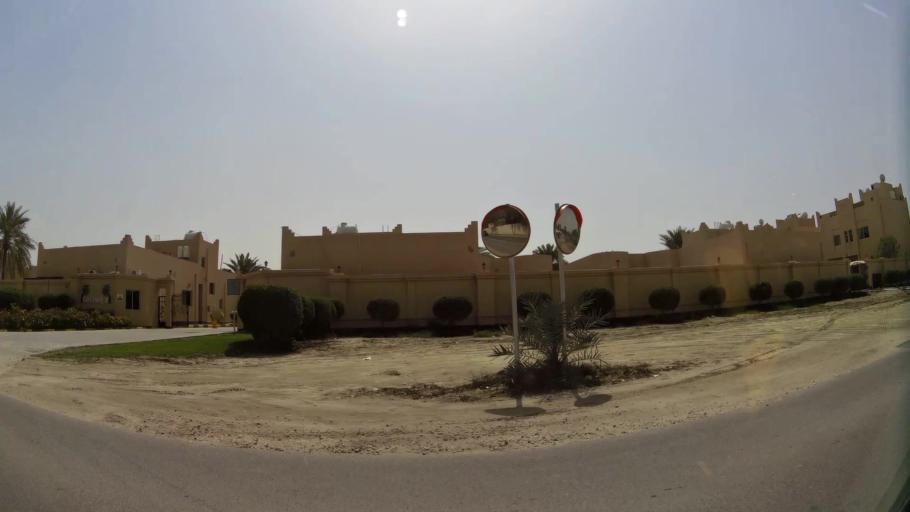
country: BH
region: Manama
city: Jidd Hafs
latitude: 26.2234
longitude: 50.4732
